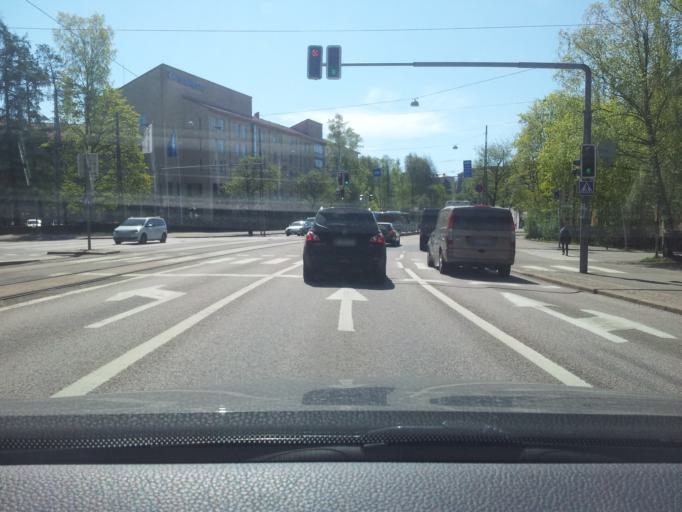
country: FI
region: Uusimaa
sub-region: Helsinki
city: Helsinki
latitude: 60.1991
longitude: 24.9009
